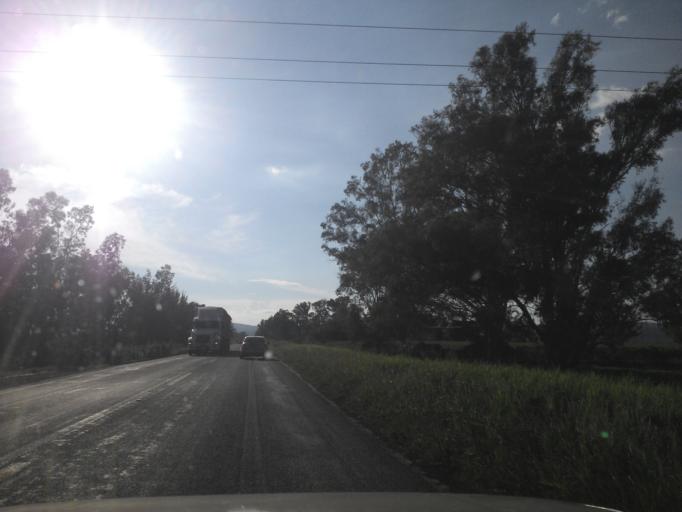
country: MX
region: Jalisco
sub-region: Tototlan
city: Nuevo Refugio de Afuera (Nuevo Refugio)
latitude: 20.5585
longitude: -102.7235
